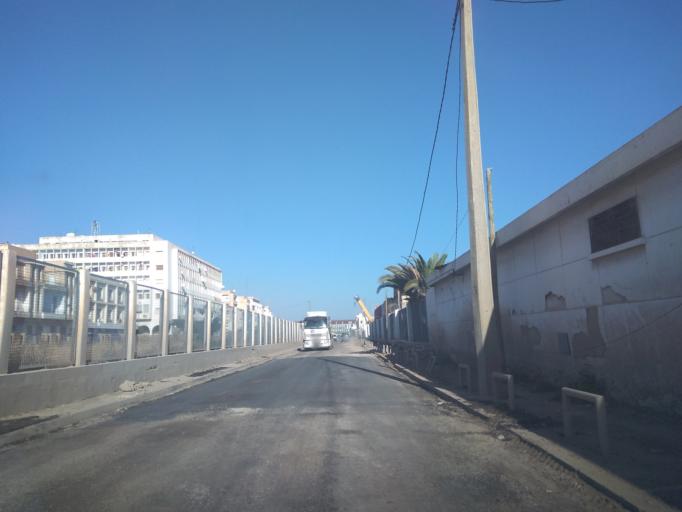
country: TN
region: Safaqis
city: Sfax
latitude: 34.7295
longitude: 10.7657
